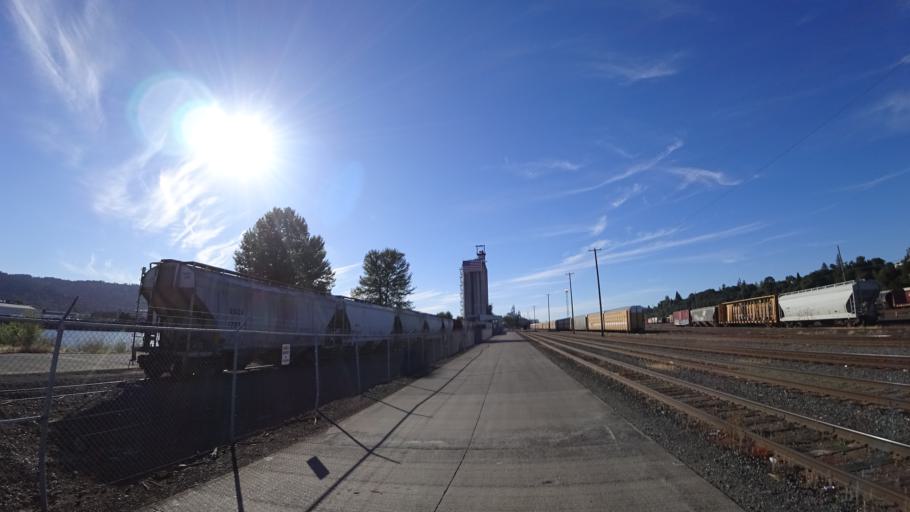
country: US
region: Oregon
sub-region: Multnomah County
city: Portland
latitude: 45.5438
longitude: -122.6870
